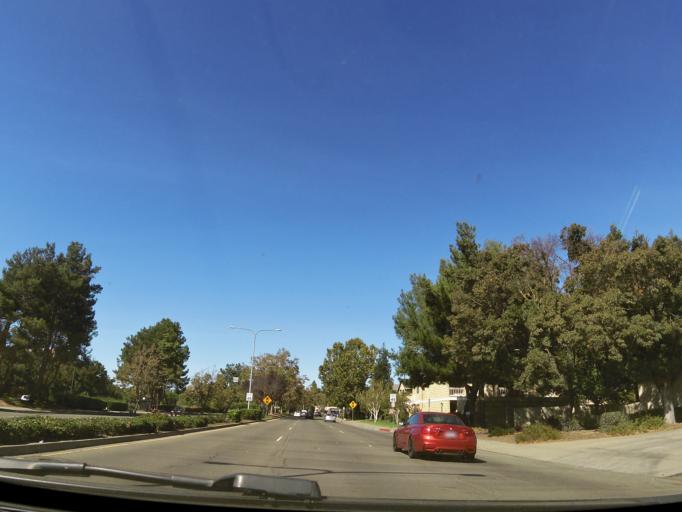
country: US
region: California
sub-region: Alameda County
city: Pleasanton
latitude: 37.6923
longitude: -121.8784
